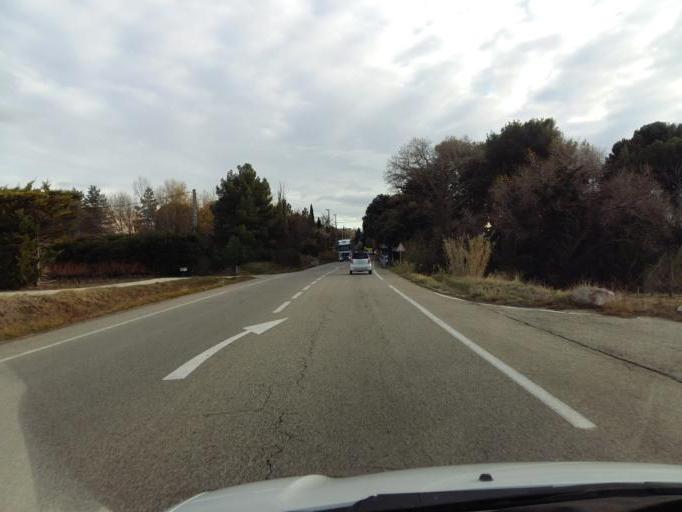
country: FR
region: Provence-Alpes-Cote d'Azur
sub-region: Departement du Vaucluse
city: Visan
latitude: 44.3205
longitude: 4.9478
